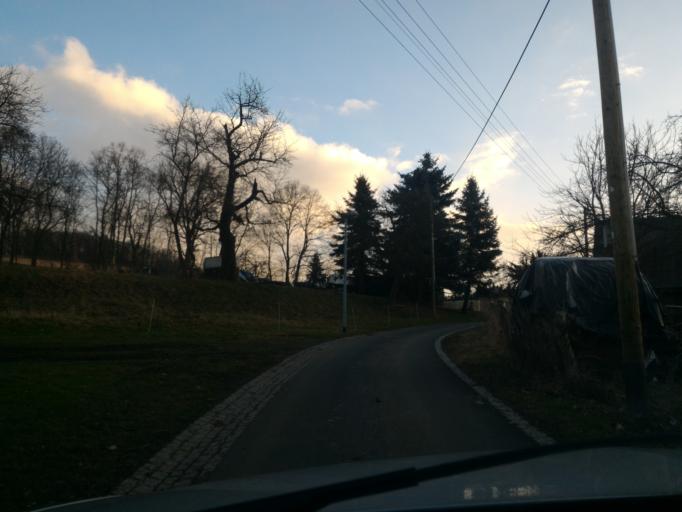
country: DE
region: Saxony
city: Hainewalde
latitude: 50.9133
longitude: 14.7096
